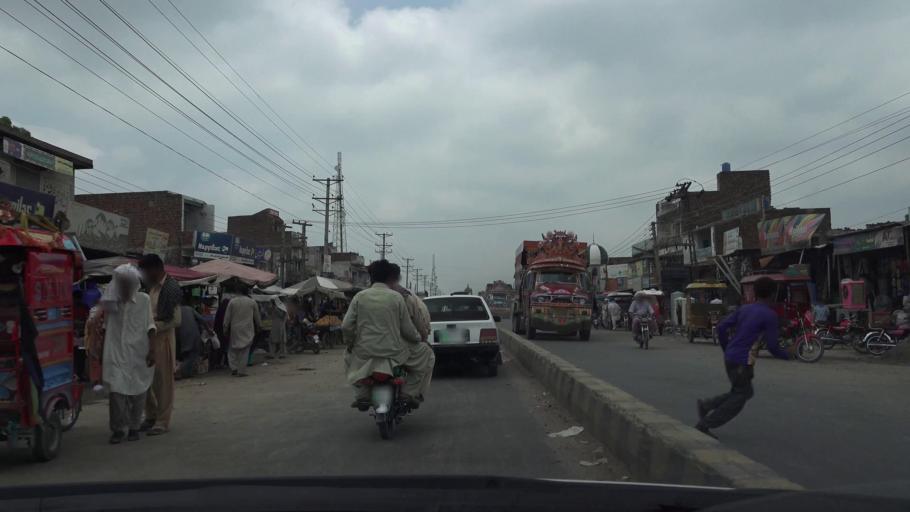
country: PK
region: Punjab
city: Faisalabad
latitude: 31.3884
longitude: 73.1973
